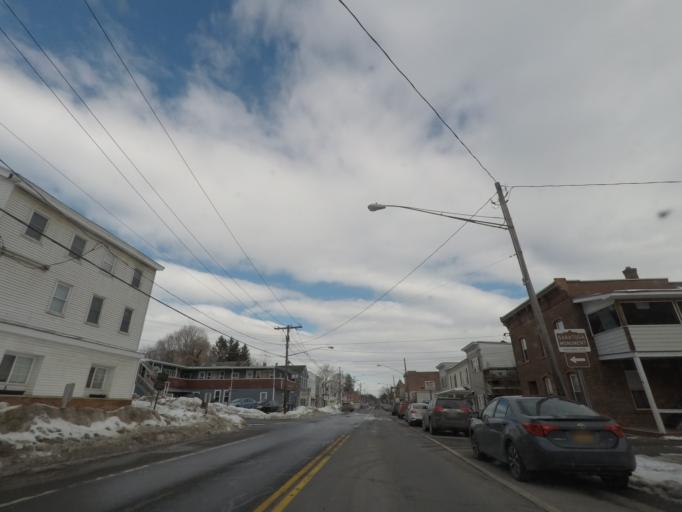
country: US
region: New York
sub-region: Saratoga County
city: Schuylerville
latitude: 43.0975
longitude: -73.5823
